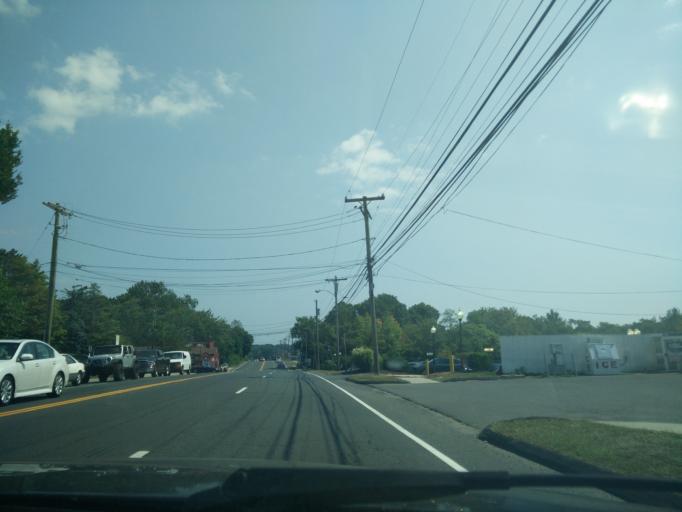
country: US
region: Connecticut
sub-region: Fairfield County
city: Southport
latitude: 41.1382
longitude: -73.2997
